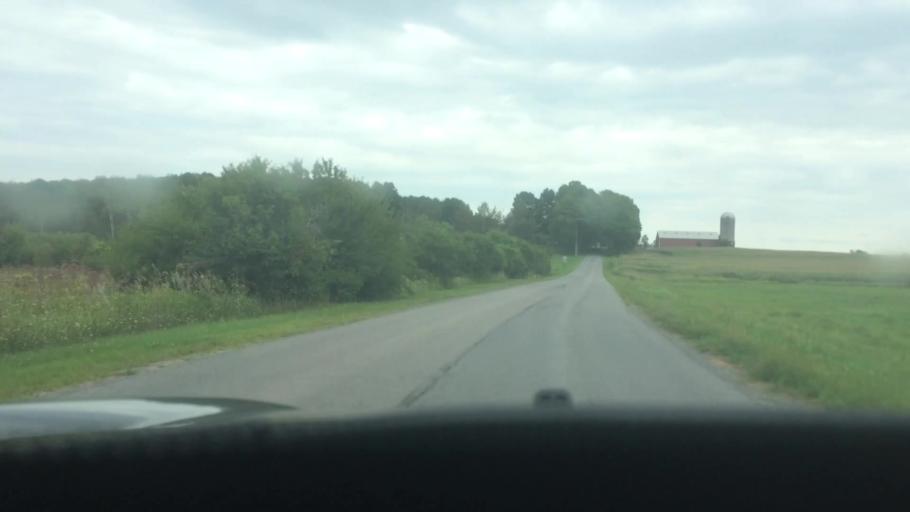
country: US
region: New York
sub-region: St. Lawrence County
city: Canton
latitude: 44.5558
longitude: -75.1314
